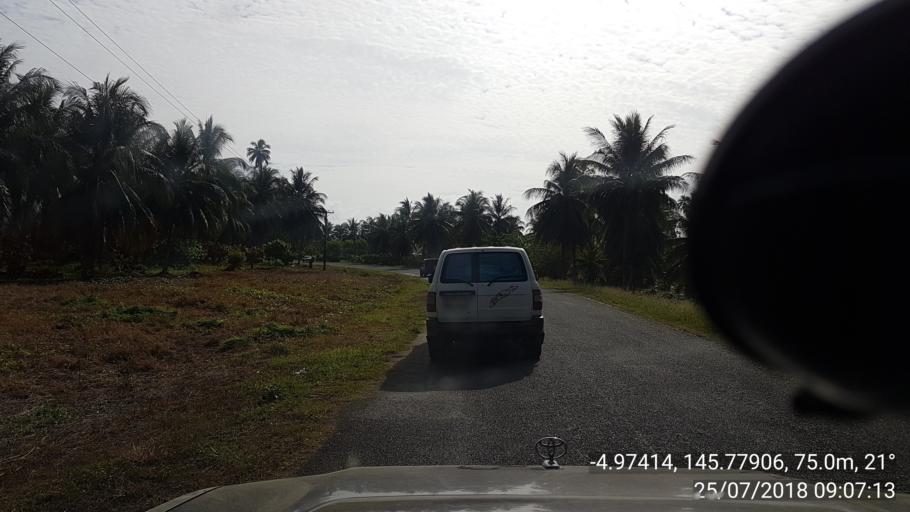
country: PG
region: Madang
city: Madang
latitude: -4.9735
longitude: 145.7799
